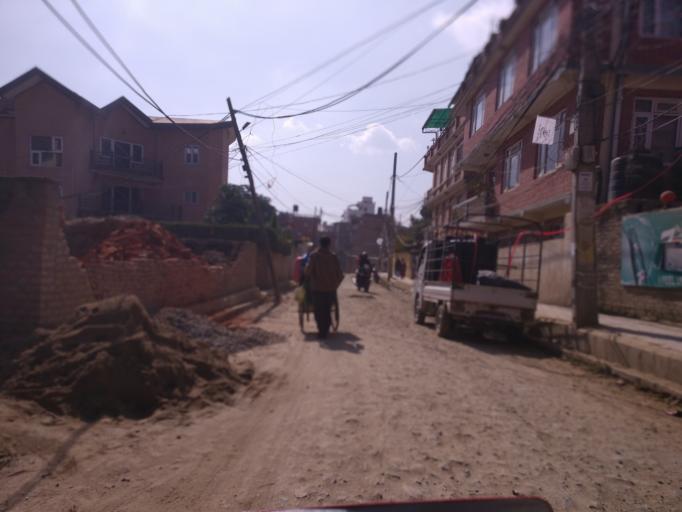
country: NP
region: Central Region
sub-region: Bagmati Zone
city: Patan
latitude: 27.6673
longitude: 85.3164
